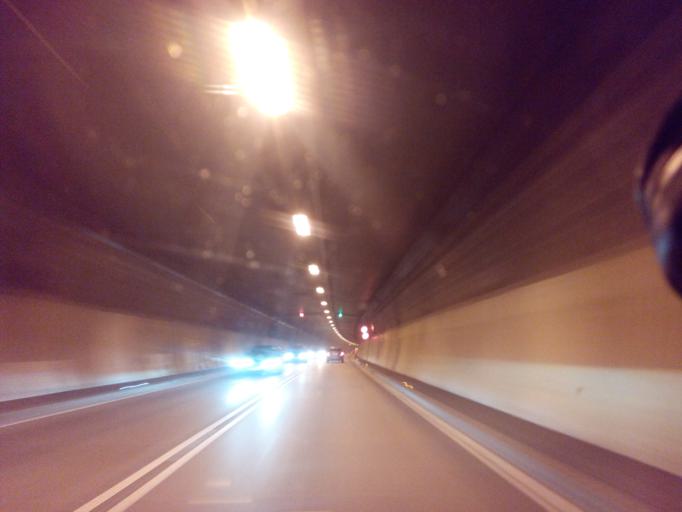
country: SK
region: Kosicky
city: Krompachy
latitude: 48.9965
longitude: 20.9027
